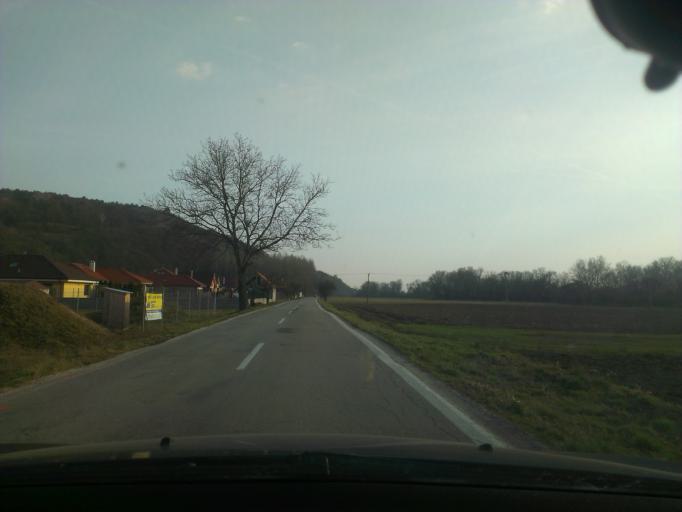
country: SK
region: Trenciansky
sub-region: Okres Nove Mesto nad Vahom
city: Nove Mesto nad Vahom
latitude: 48.6944
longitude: 17.8805
